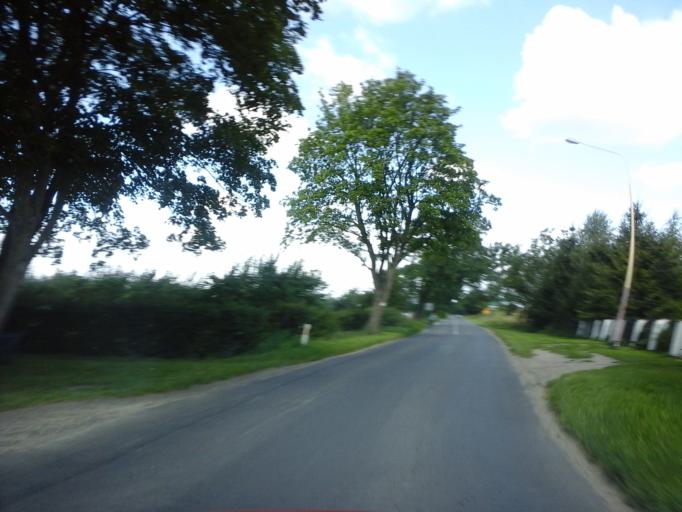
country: PL
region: West Pomeranian Voivodeship
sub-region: Powiat stargardzki
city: Dolice
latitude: 53.1927
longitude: 15.1937
